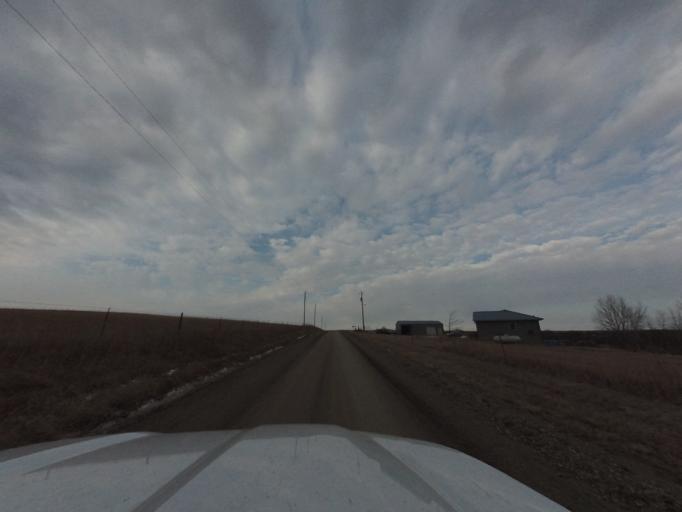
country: US
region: Kansas
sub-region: Chase County
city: Cottonwood Falls
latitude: 38.4492
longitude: -96.3830
